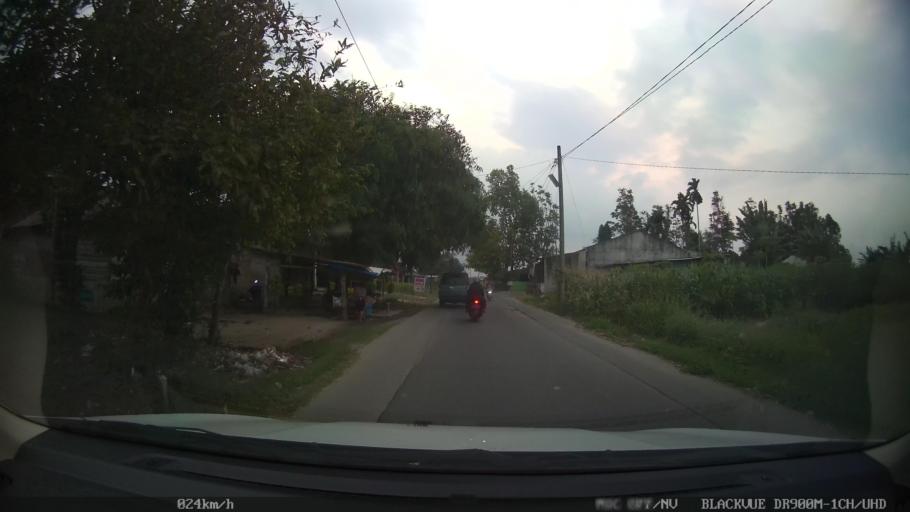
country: ID
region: North Sumatra
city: Sunggal
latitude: 3.5613
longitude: 98.5949
